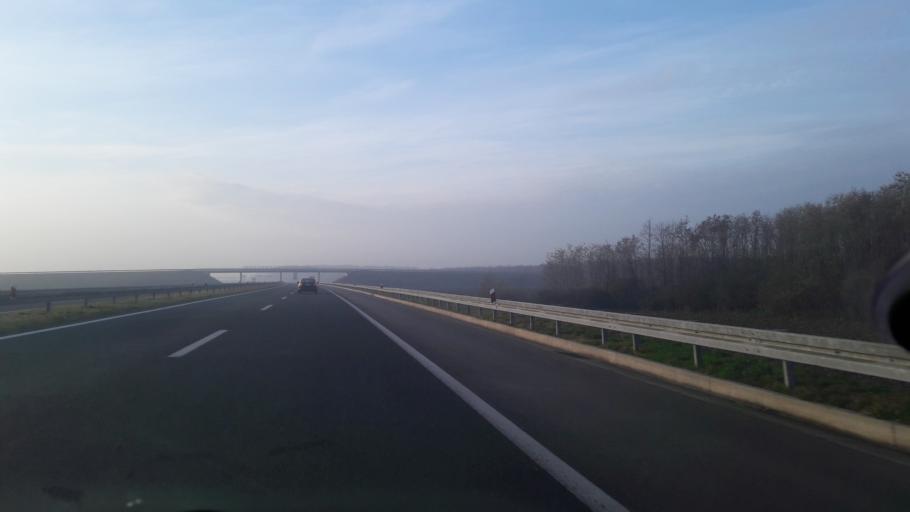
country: HR
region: Osjecko-Baranjska
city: Cepin
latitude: 45.5195
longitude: 18.5094
